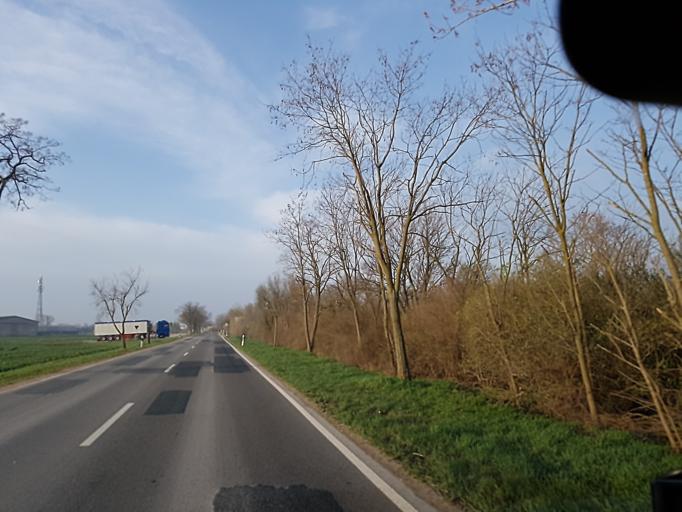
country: DE
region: Brandenburg
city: Muhlberg
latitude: 51.4286
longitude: 13.2677
